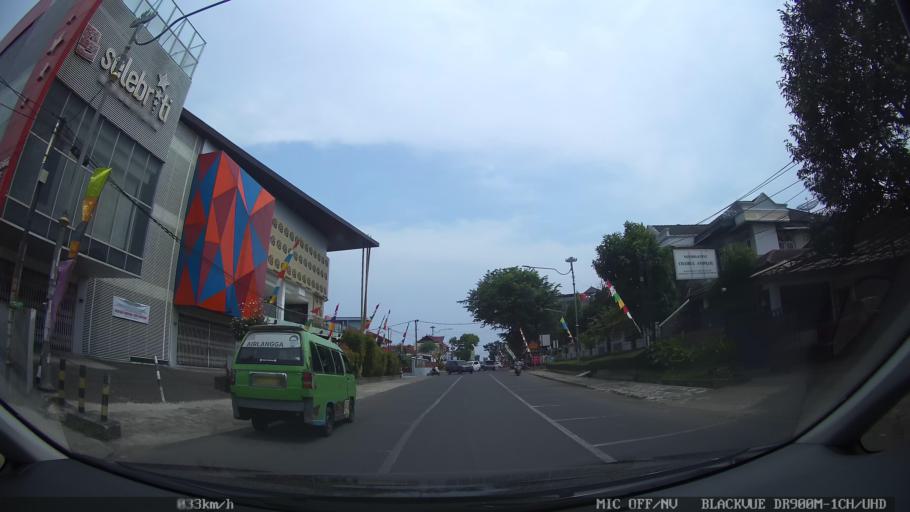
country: ID
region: Lampung
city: Bandarlampung
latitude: -5.4272
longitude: 105.2757
